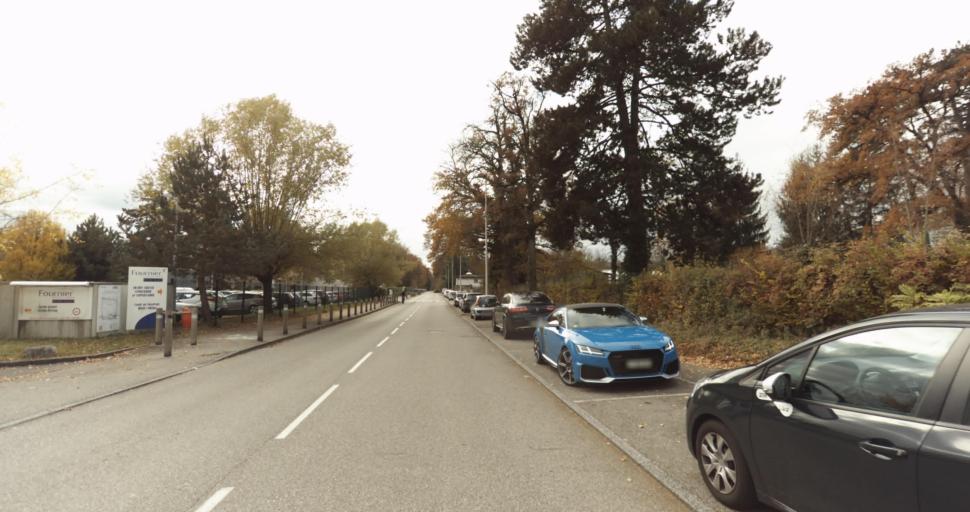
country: FR
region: Rhone-Alpes
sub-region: Departement de la Haute-Savoie
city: Metz-Tessy
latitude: 45.9284
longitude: 6.1153
